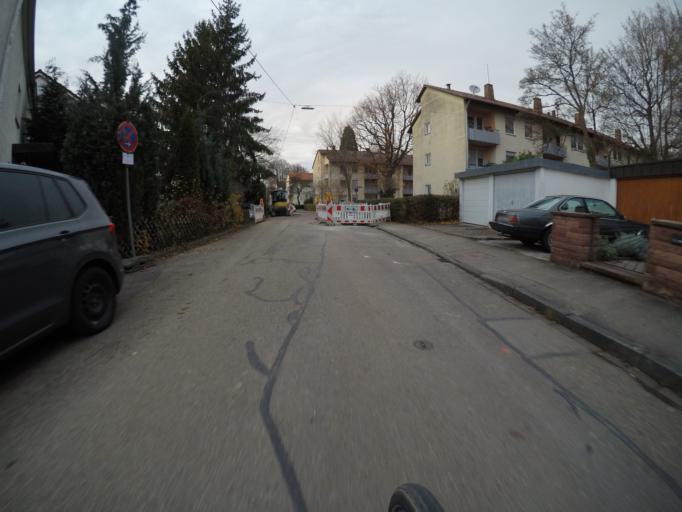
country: DE
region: Baden-Wuerttemberg
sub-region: Regierungsbezirk Stuttgart
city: Ostfildern
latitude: 48.7300
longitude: 9.2608
